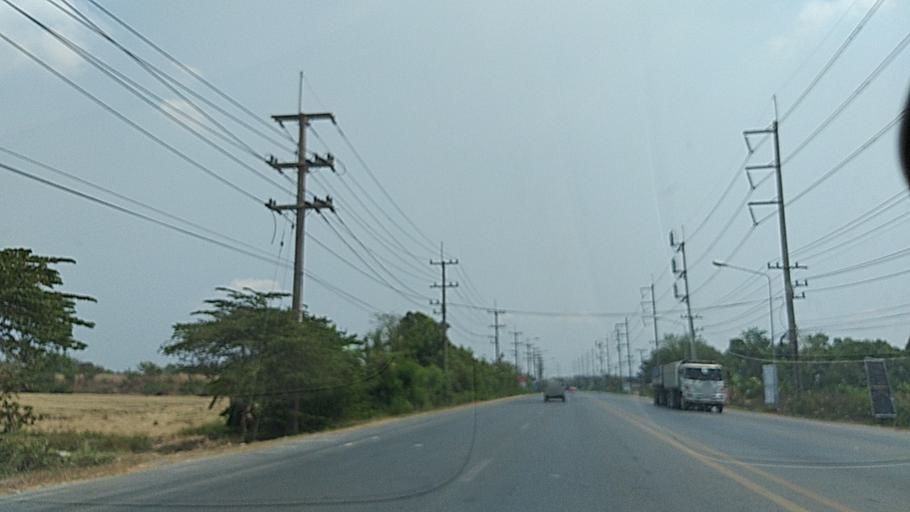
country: TH
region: Bangkok
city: Nong Chok
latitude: 13.9612
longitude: 100.8988
